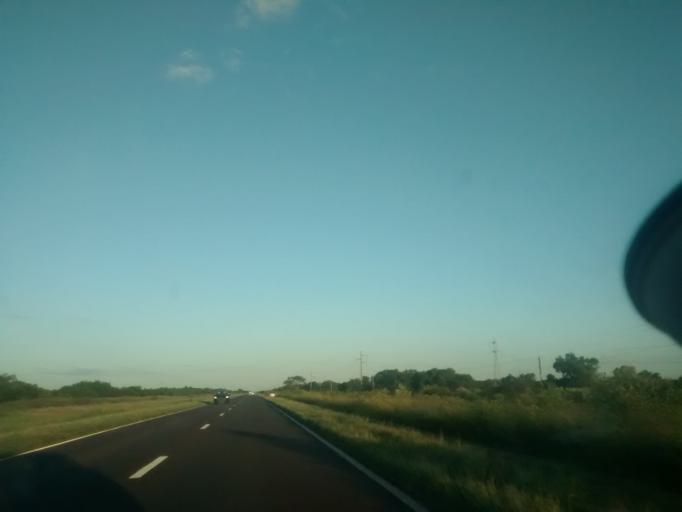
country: AR
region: Chaco
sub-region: Departamento de Presidencia de la Plaza
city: Presidencia de la Plaza
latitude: -27.0795
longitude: -59.6641
